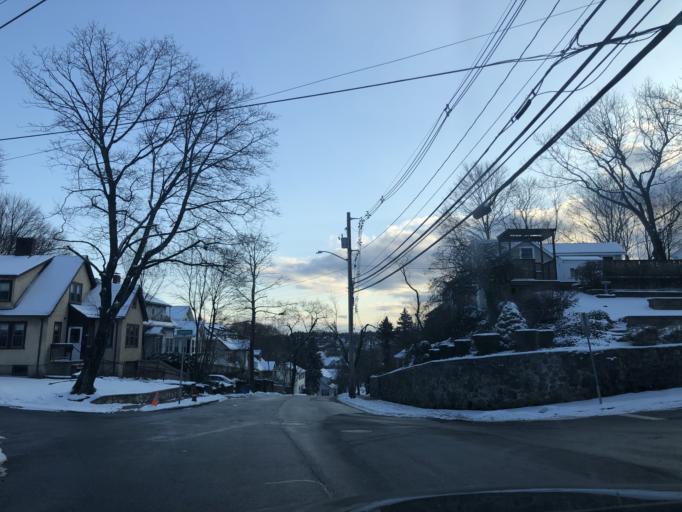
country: US
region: Massachusetts
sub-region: Middlesex County
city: Arlington
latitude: 42.4263
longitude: -71.1691
